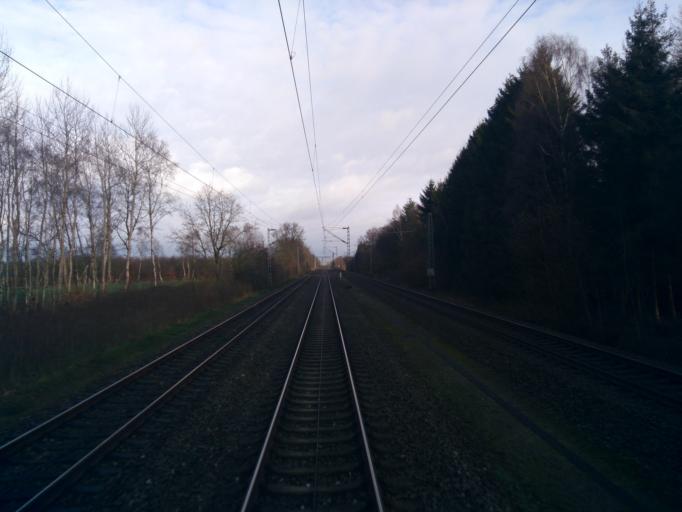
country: DE
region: Lower Saxony
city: Vahlde
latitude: 53.2196
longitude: 9.6187
